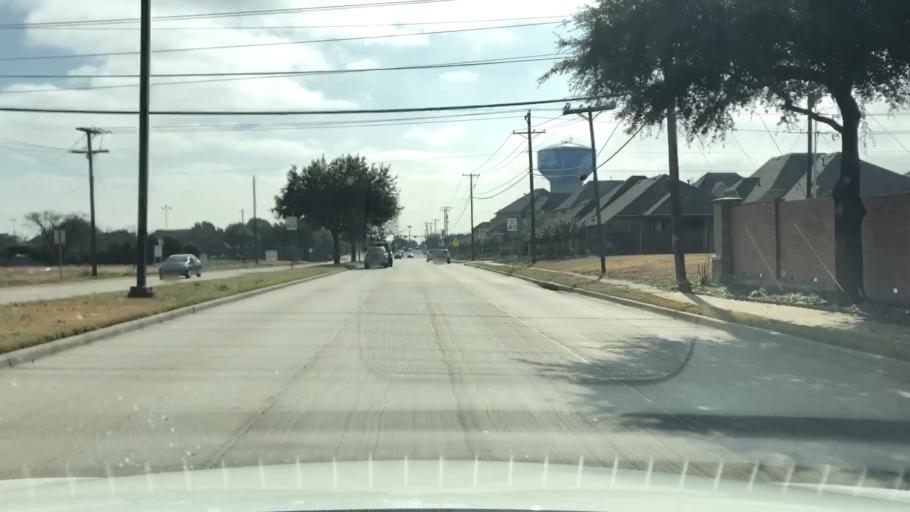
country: US
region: Texas
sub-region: Dallas County
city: Addison
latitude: 32.9768
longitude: -96.8558
